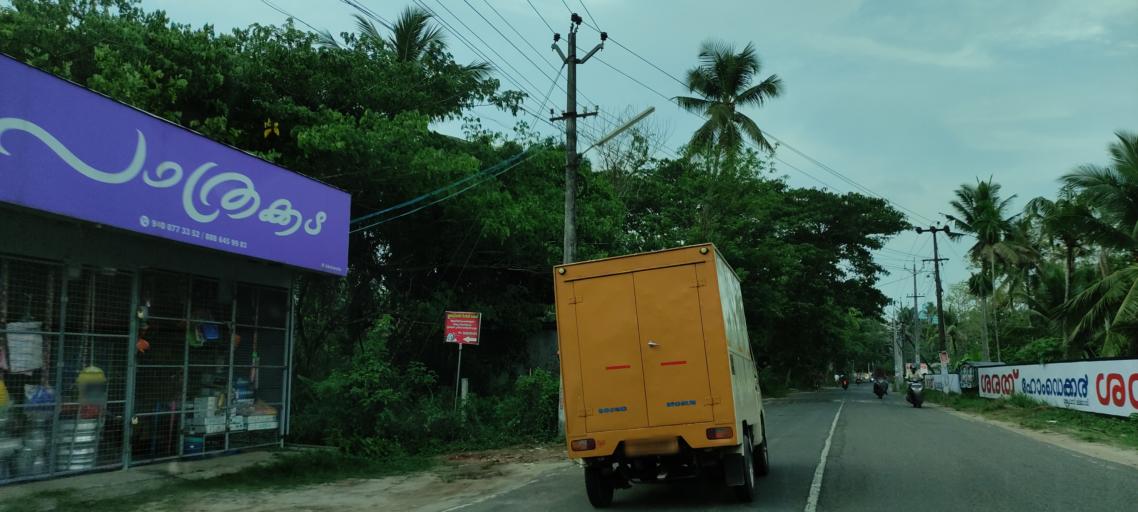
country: IN
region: Kerala
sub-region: Kottayam
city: Vaikam
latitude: 9.7534
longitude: 76.3634
